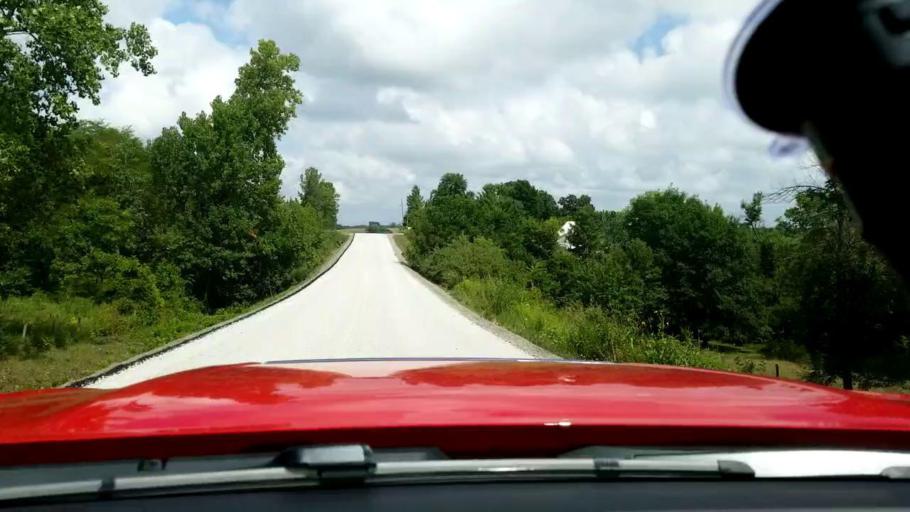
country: US
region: Iowa
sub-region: Decatur County
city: Lamoni
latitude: 40.6443
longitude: -94.0530
